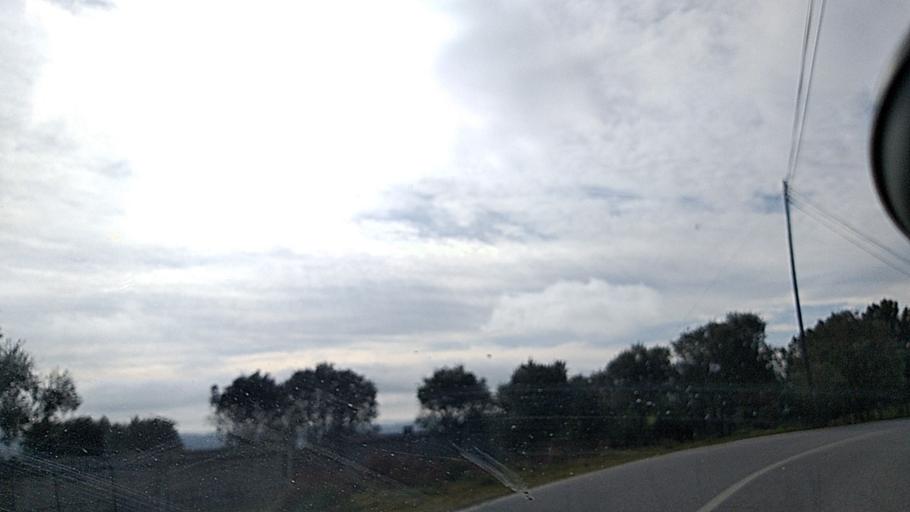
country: PT
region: Guarda
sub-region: Aguiar da Beira
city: Aguiar da Beira
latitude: 40.7574
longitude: -7.5426
